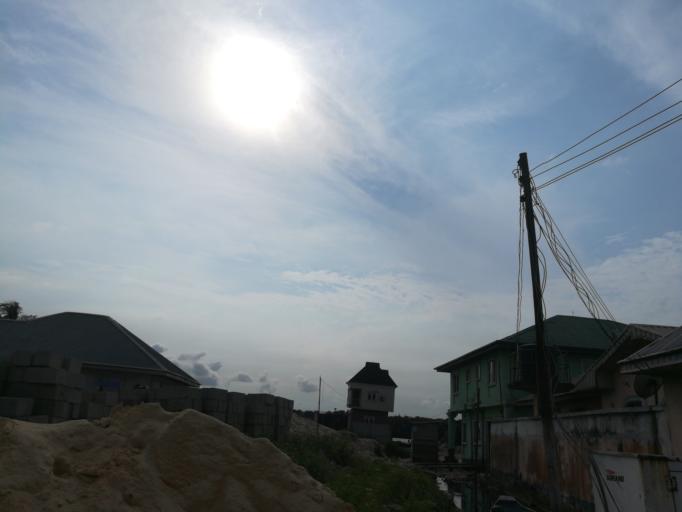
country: NG
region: Rivers
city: Okrika
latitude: 4.7340
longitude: 7.0854
